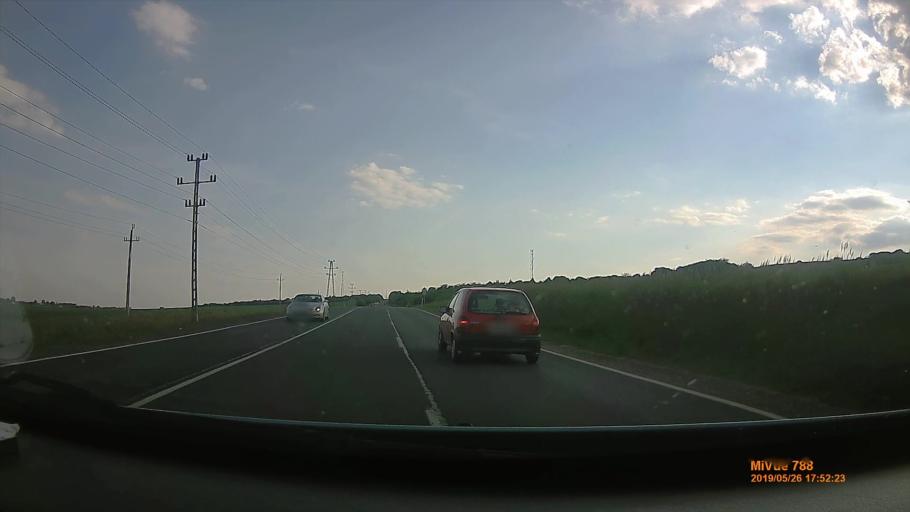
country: HU
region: Borsod-Abauj-Zemplen
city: Szikszo
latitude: 48.1653
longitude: 20.9070
